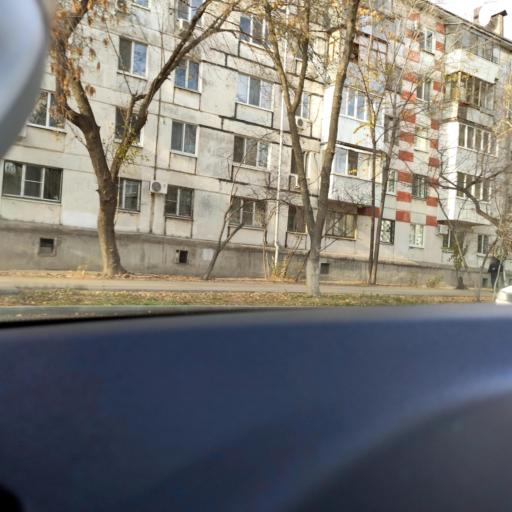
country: RU
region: Samara
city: Samara
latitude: 53.1922
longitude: 50.1309
